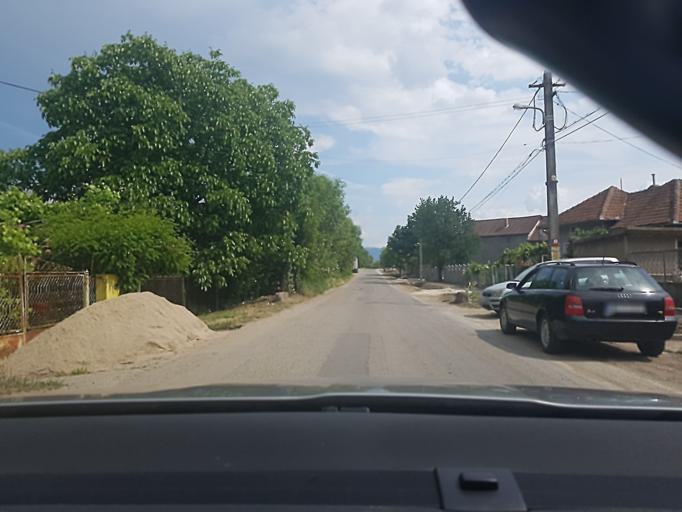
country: RO
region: Hunedoara
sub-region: Comuna Calan
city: Calan
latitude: 45.7234
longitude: 23.0220
